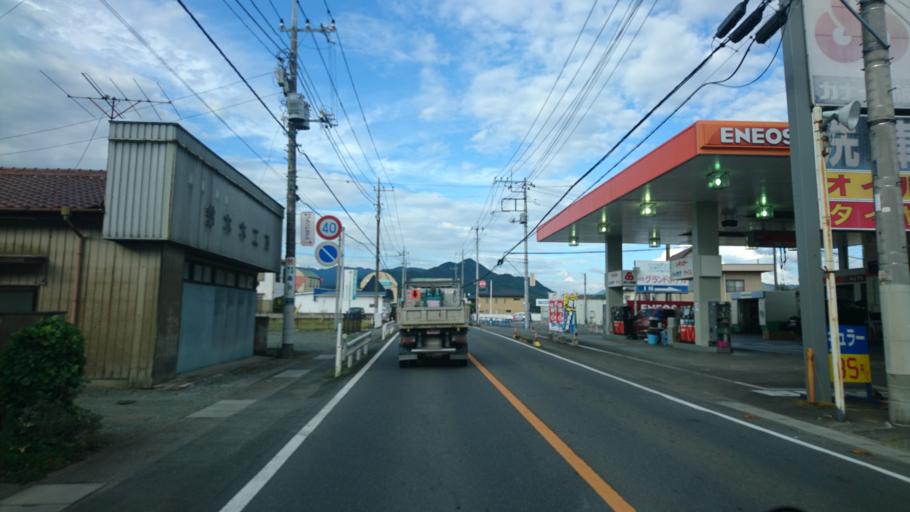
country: JP
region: Gunma
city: Kiryu
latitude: 36.4069
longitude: 139.3031
